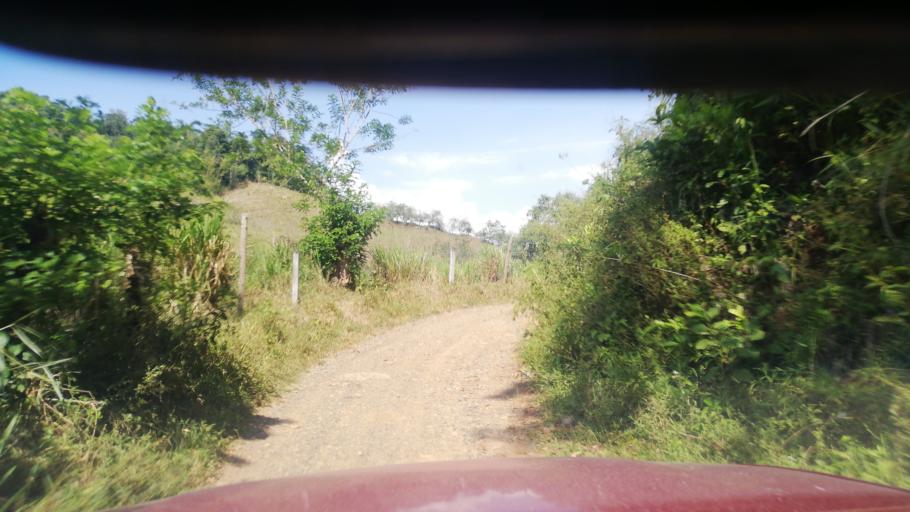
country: CO
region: Risaralda
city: Balboa
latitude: 4.9020
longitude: -75.9395
